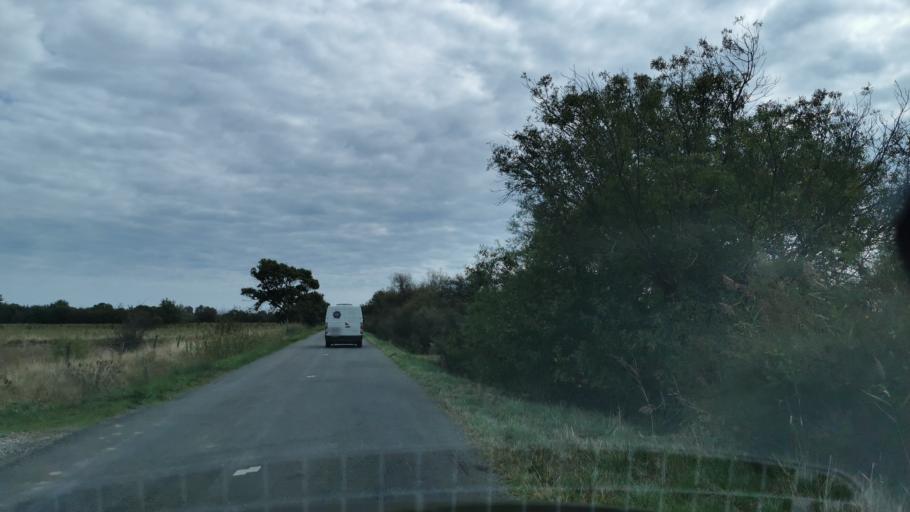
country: FR
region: Languedoc-Roussillon
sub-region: Departement de l'Herault
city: Vendres
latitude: 43.2317
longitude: 3.1981
